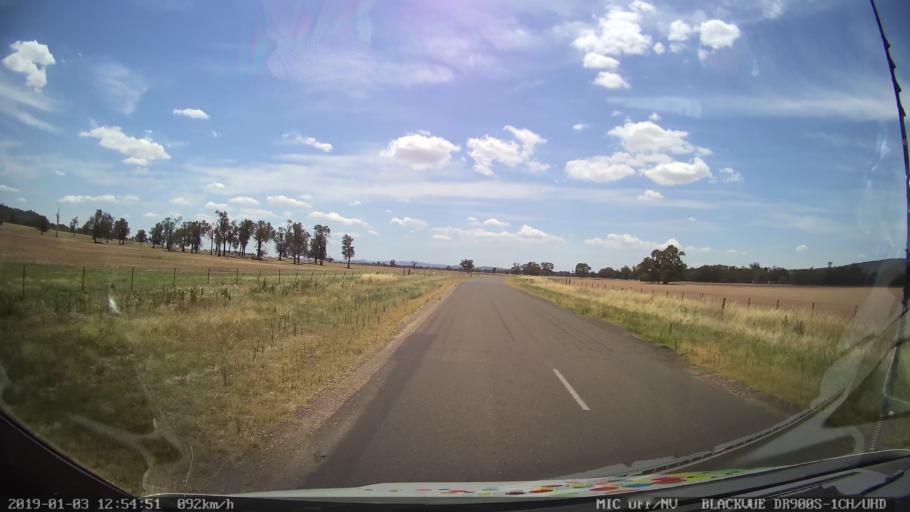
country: AU
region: New South Wales
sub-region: Weddin
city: Grenfell
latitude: -33.6487
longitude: 148.3222
